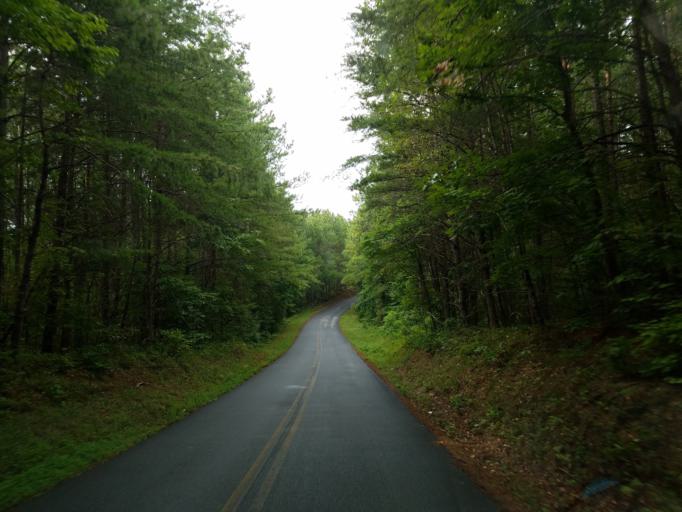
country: US
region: Georgia
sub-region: Bartow County
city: Rydal
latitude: 34.3784
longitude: -84.6716
